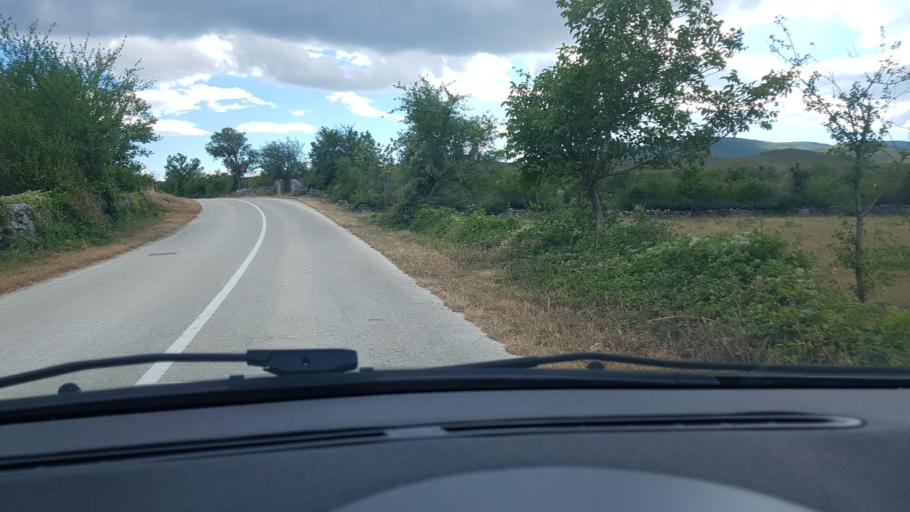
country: HR
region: Sibensko-Kniniska
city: Kistanje
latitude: 44.1007
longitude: 15.9380
